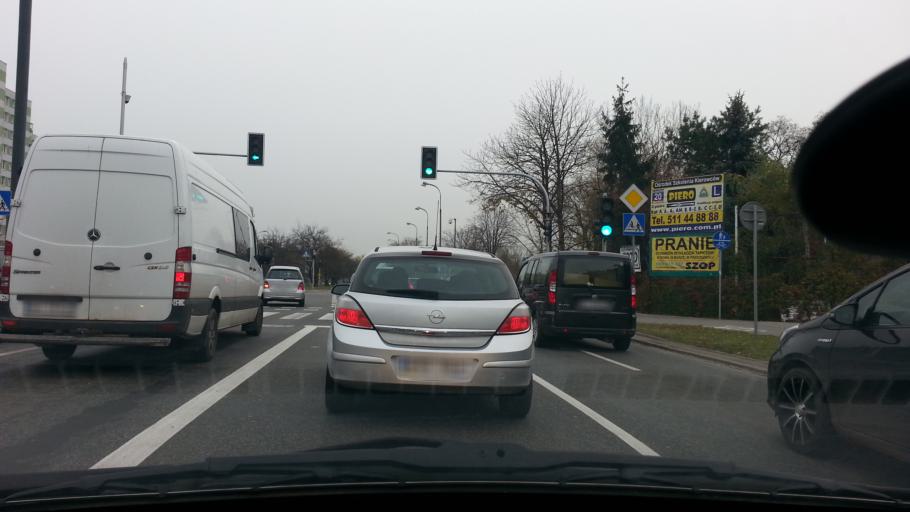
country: PL
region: Masovian Voivodeship
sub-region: Warszawa
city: Targowek
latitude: 52.2916
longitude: 21.0179
